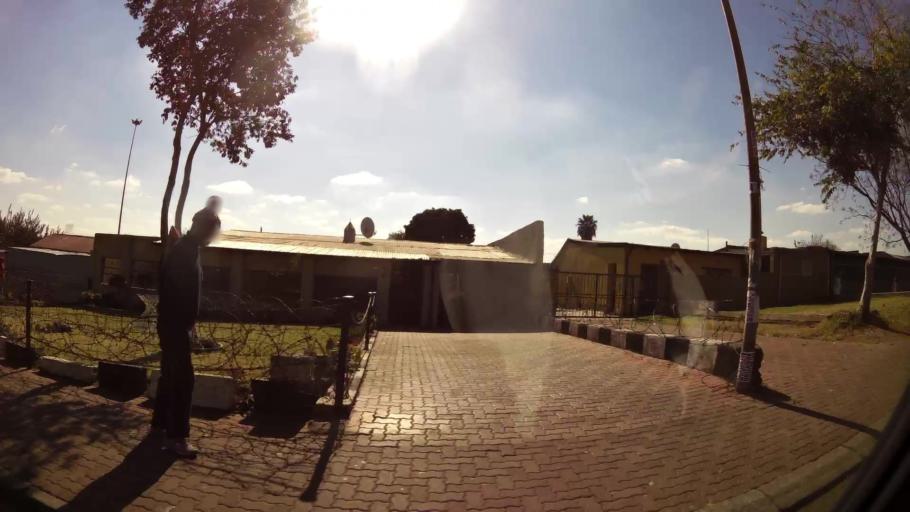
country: ZA
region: Gauteng
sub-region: City of Johannesburg Metropolitan Municipality
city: Soweto
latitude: -26.2438
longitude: 27.9160
